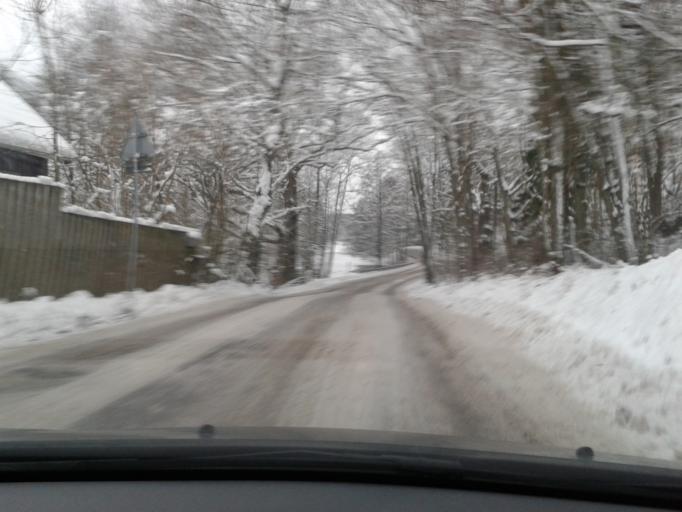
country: SE
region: Stockholm
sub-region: Nacka Kommun
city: Saltsjobaden
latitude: 59.2301
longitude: 18.2991
